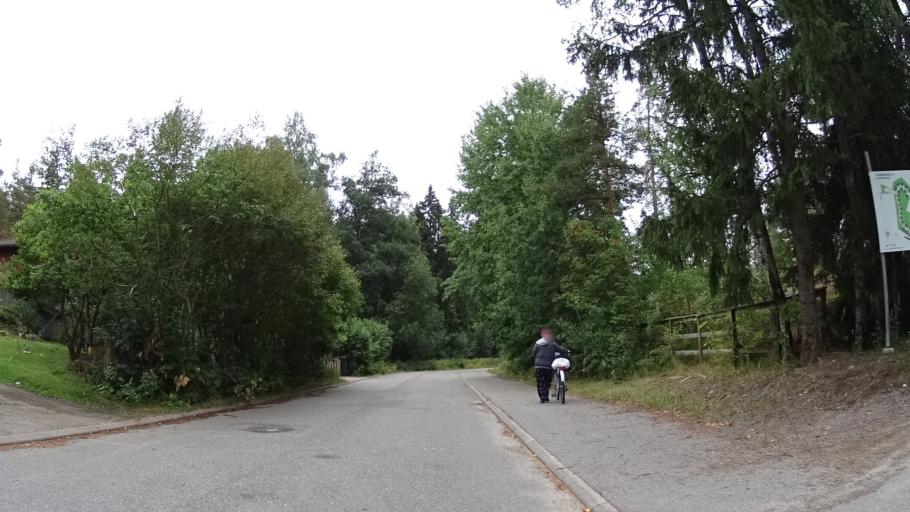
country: FI
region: Uusimaa
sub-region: Helsinki
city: Kilo
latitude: 60.1961
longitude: 24.7593
